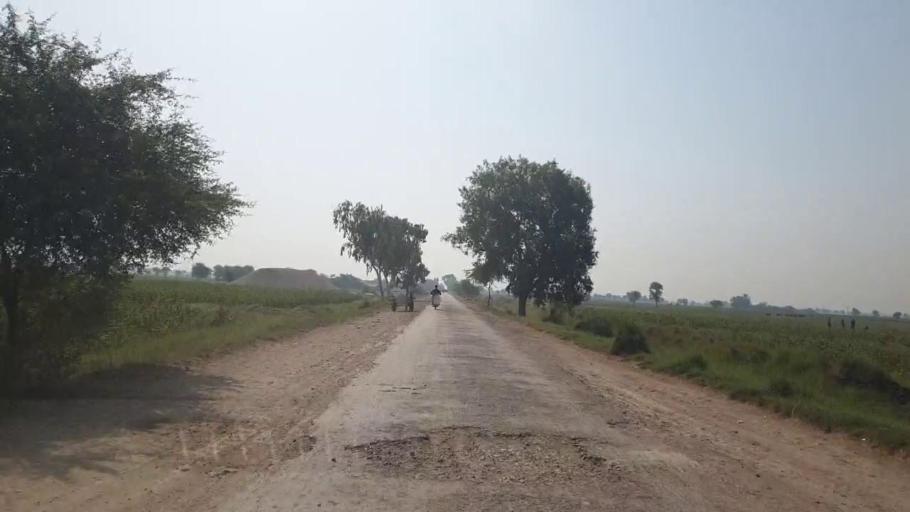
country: PK
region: Sindh
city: Shahdadpur
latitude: 25.9322
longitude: 68.7305
